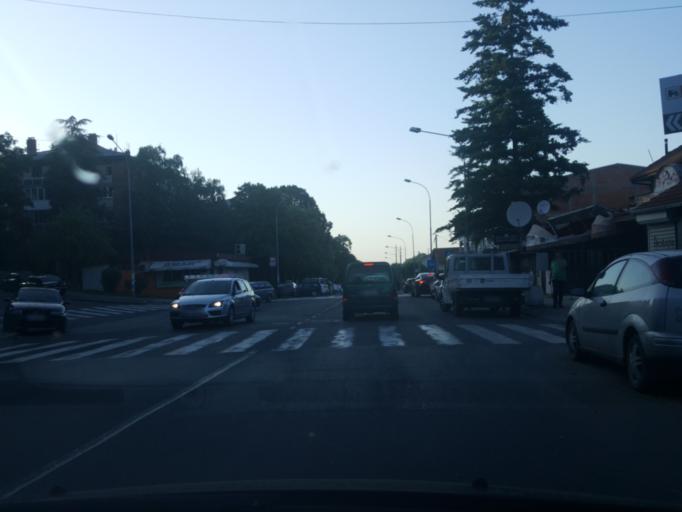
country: RS
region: Central Serbia
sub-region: Belgrade
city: Palilula
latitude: 44.8047
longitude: 20.5250
